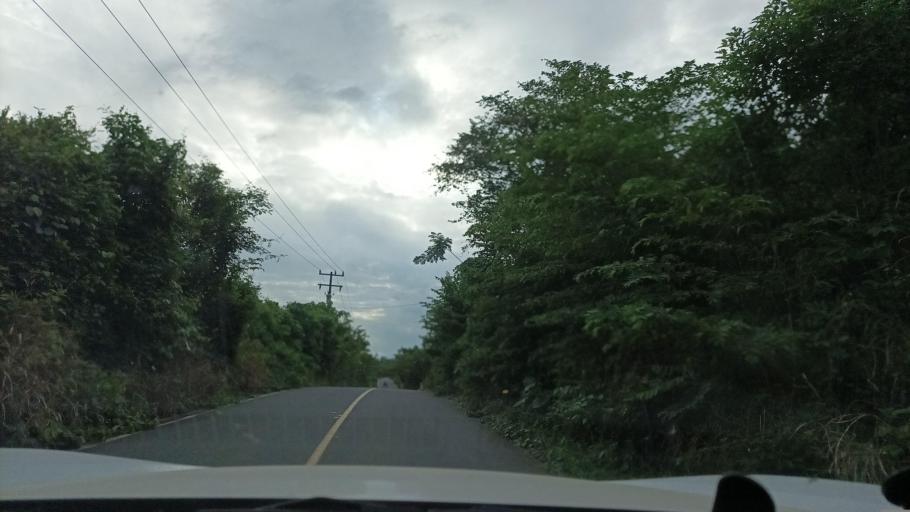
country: MX
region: Veracruz
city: Hidalgotitlan
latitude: 17.7165
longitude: -94.4753
